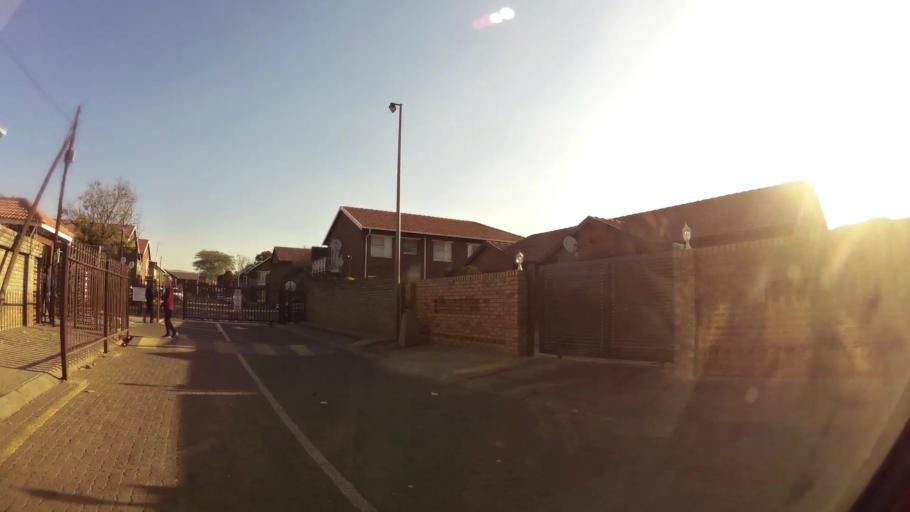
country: ZA
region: North-West
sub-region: Bojanala Platinum District Municipality
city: Rustenburg
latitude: -25.6450
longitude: 27.2239
